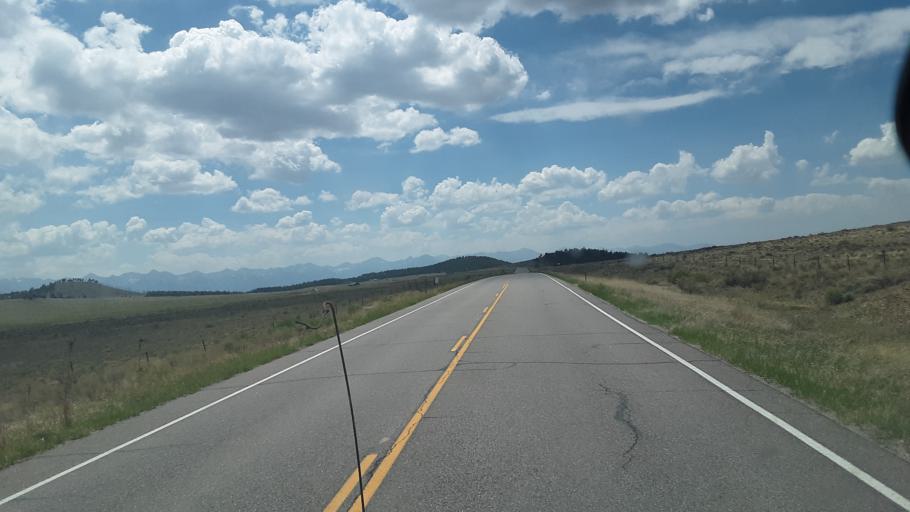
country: US
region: Colorado
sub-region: Custer County
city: Westcliffe
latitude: 38.1648
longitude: -105.2780
